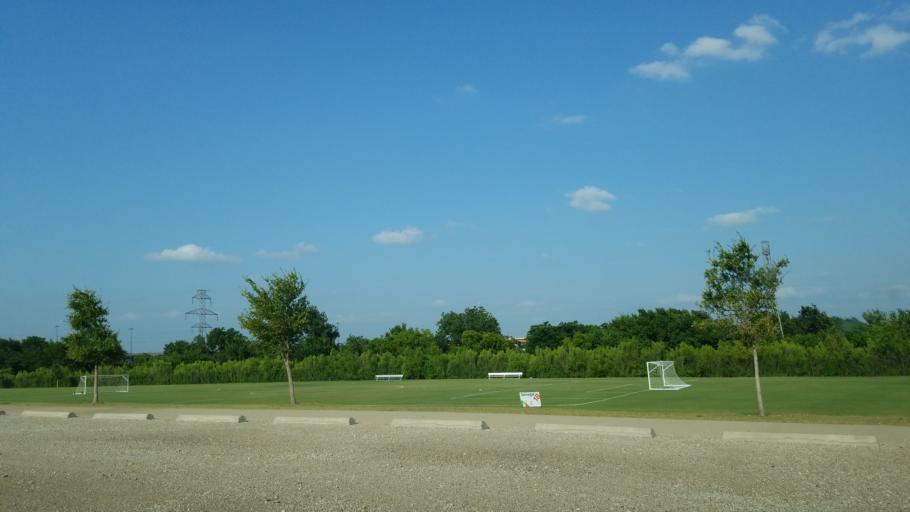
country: US
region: Texas
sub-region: Dallas County
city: Farmers Branch
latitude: 32.8786
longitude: -96.9049
